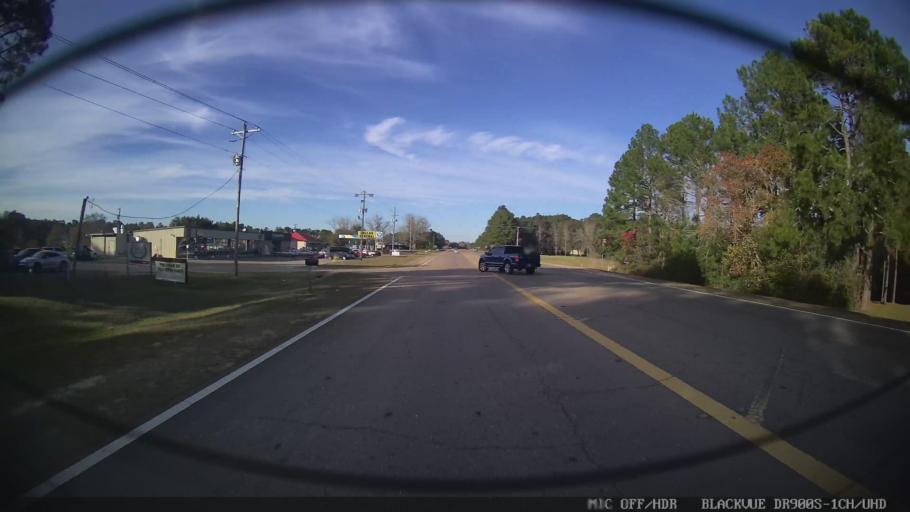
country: US
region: Mississippi
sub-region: Forrest County
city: Hattiesburg
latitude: 31.2356
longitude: -89.3023
